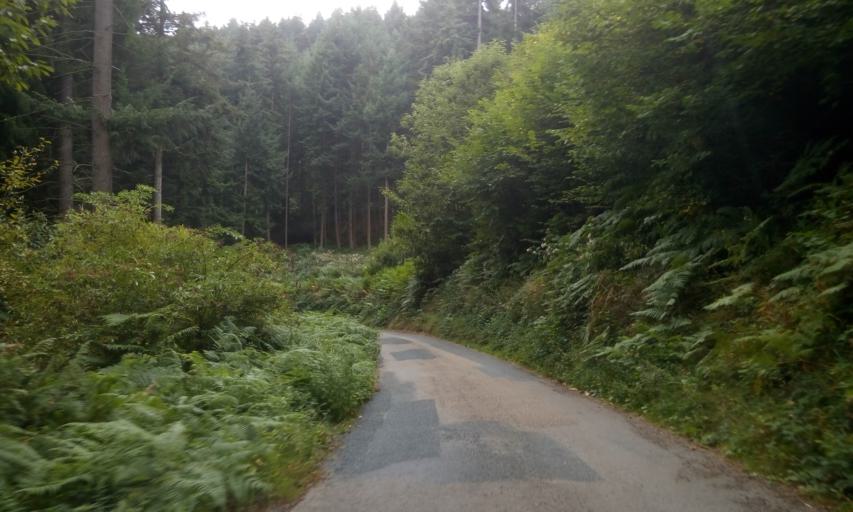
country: FR
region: Rhone-Alpes
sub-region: Departement du Rhone
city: Grandris
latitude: 45.9898
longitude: 4.4366
